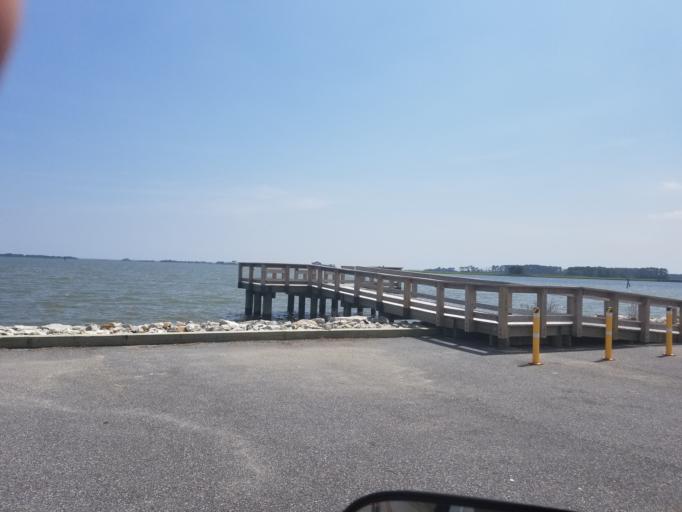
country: US
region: Maryland
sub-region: Worcester County
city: Snow Hill
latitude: 38.0766
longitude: -75.3644
